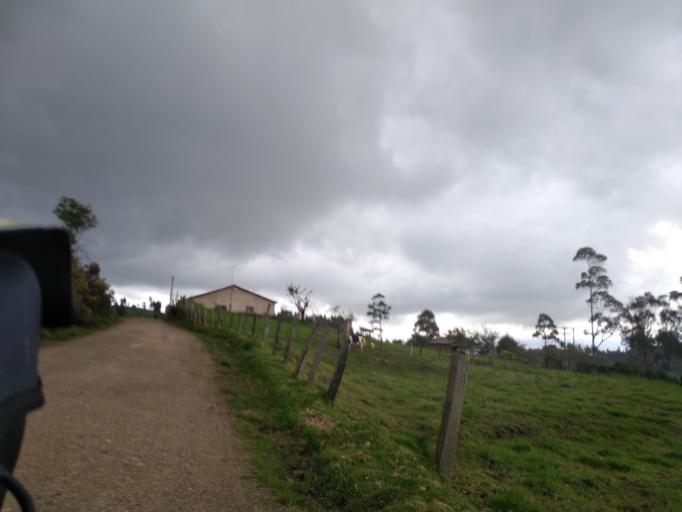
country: CO
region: Boyaca
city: Sotaquira
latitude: 5.7643
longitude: -73.2755
